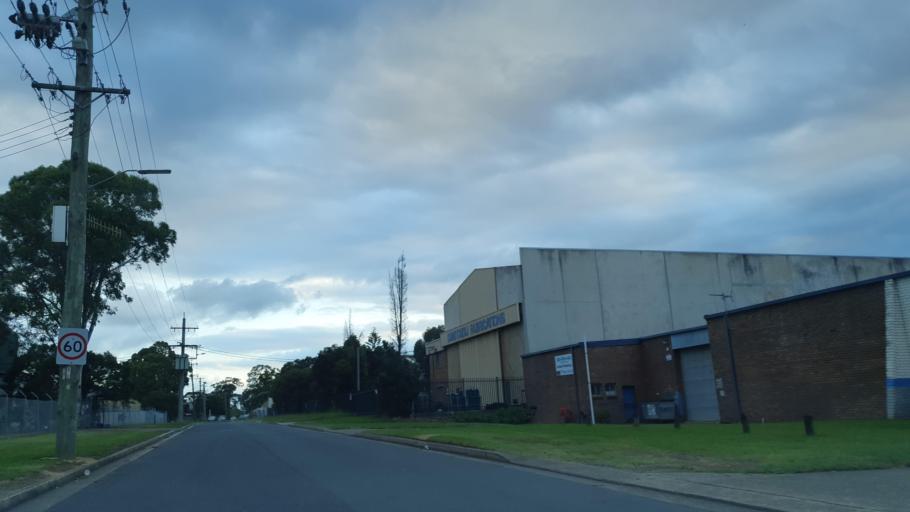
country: AU
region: New South Wales
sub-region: Penrith Municipality
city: Werrington County
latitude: -33.7389
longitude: 150.7728
